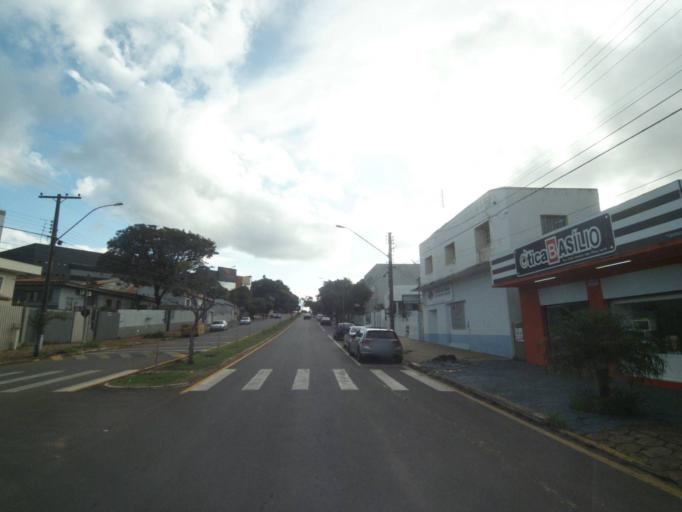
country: BR
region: Parana
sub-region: Telemaco Borba
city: Telemaco Borba
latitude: -24.3272
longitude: -50.6182
